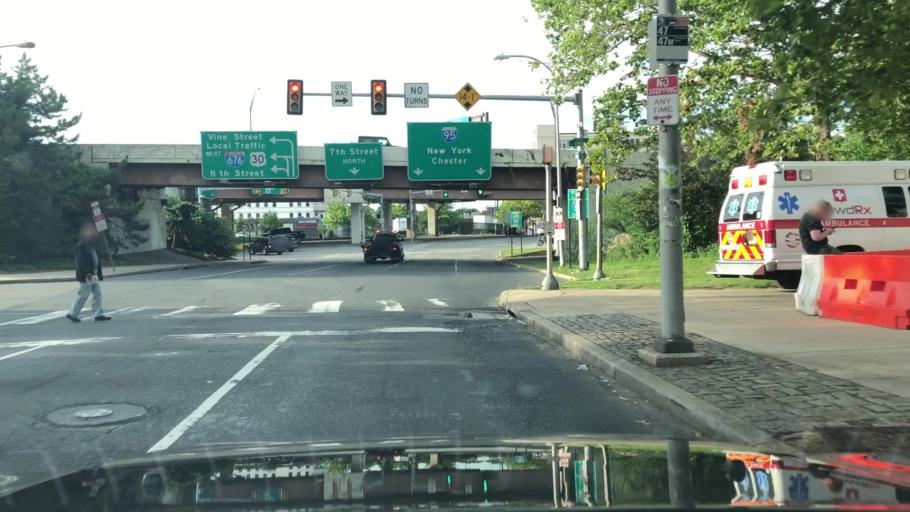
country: US
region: Pennsylvania
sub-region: Philadelphia County
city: Philadelphia
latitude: 39.9562
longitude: -75.1514
